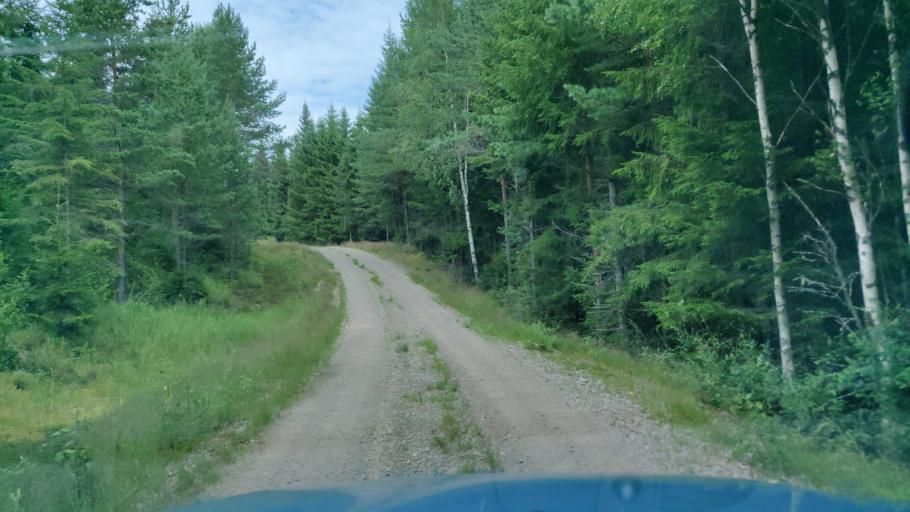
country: SE
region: Vaermland
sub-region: Hagfors Kommun
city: Hagfors
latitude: 59.9564
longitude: 13.5906
